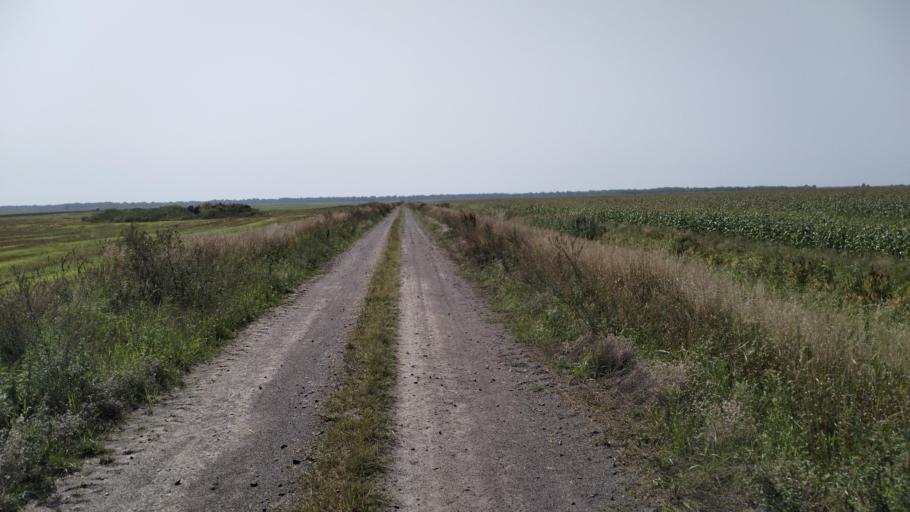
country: BY
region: Brest
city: Davyd-Haradok
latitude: 51.9900
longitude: 27.1643
